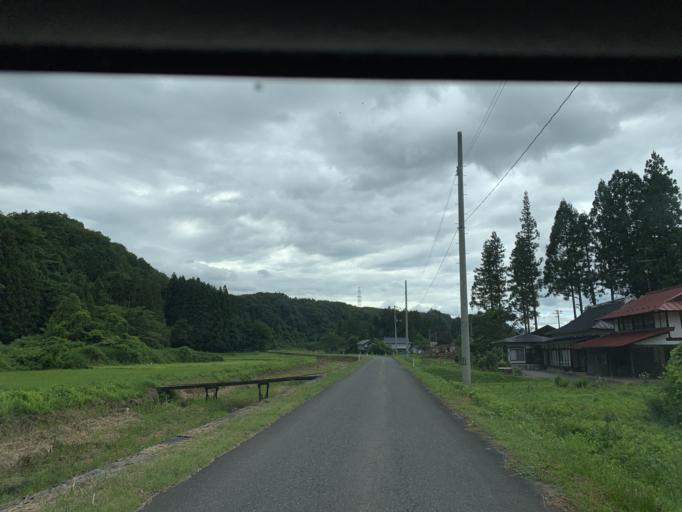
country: JP
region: Iwate
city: Ichinoseki
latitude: 38.9457
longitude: 141.0271
